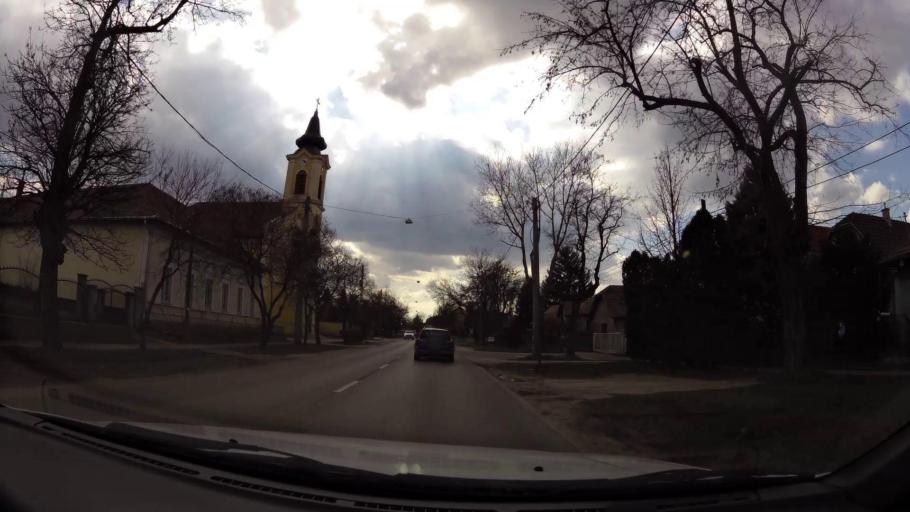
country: HU
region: Budapest
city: Budapest XVII. keruelet
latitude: 47.4903
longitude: 19.2915
